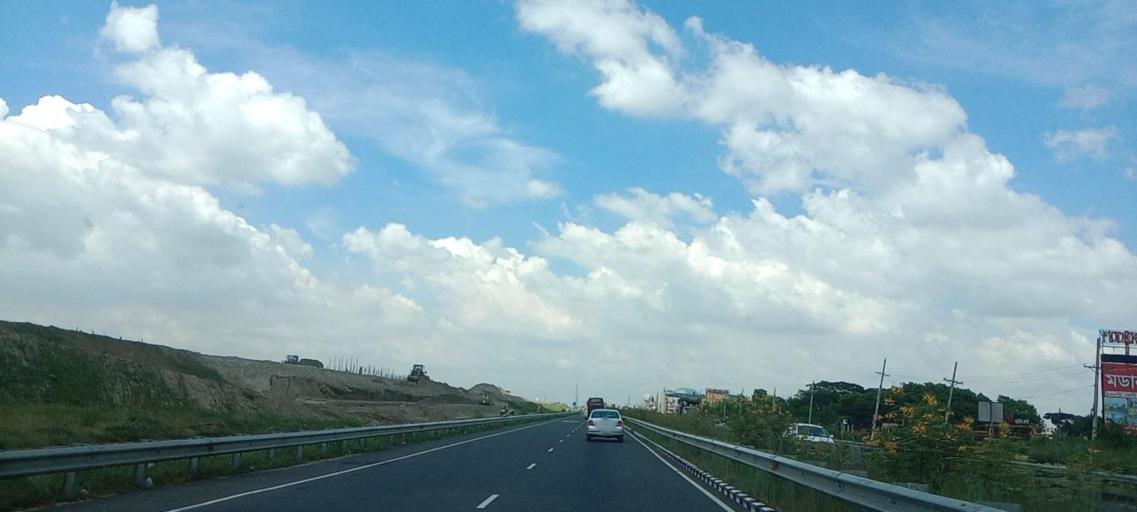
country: BD
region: Dhaka
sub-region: Dhaka
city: Dhaka
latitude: 23.6083
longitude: 90.3255
